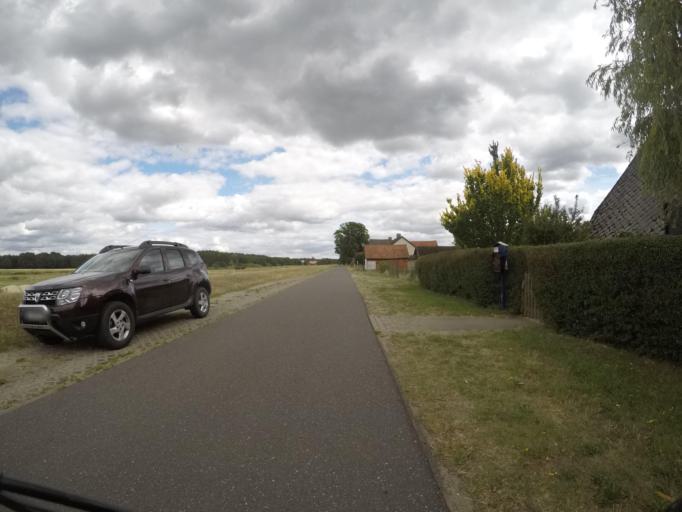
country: DE
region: Mecklenburg-Vorpommern
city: Lubtheen
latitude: 53.2991
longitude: 10.9725
